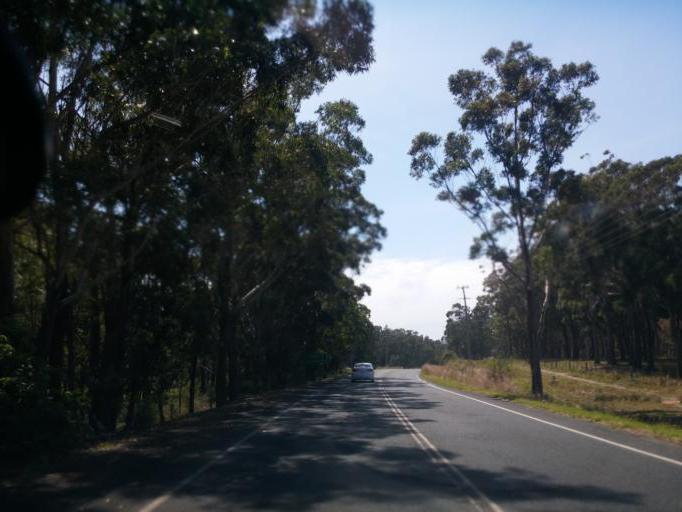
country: AU
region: New South Wales
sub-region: Great Lakes
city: Forster
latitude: -32.3567
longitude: 152.5047
